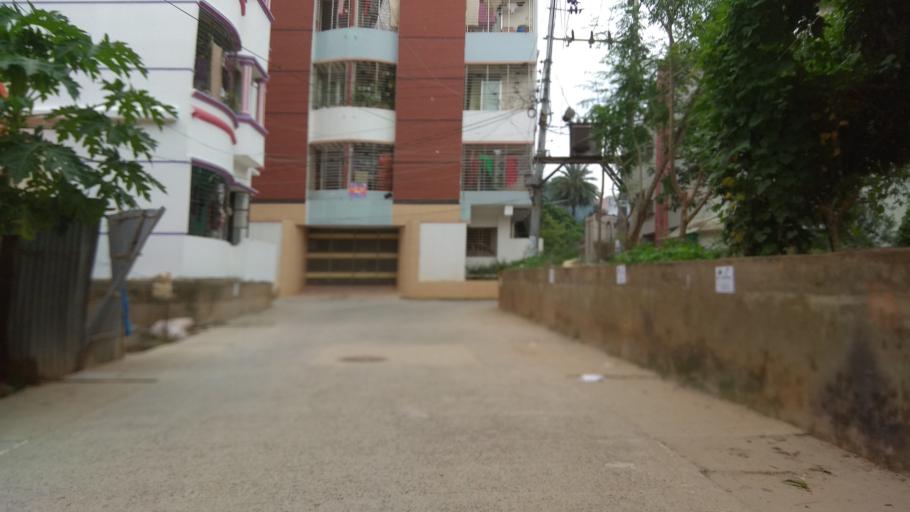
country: BD
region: Dhaka
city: Tungi
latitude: 23.8212
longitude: 90.3583
